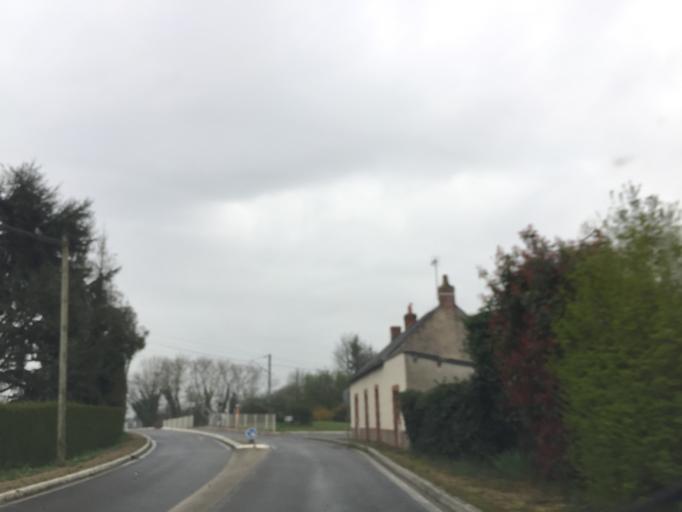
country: FR
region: Pays de la Loire
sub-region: Departement de la Loire-Atlantique
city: Casson
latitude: 47.3961
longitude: -1.5270
